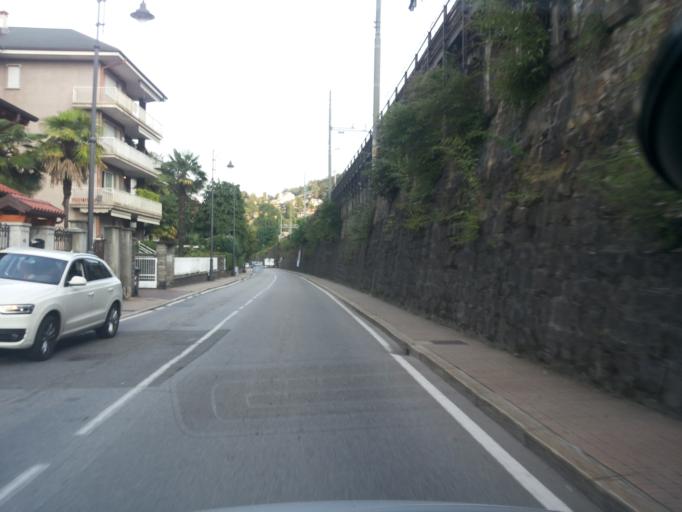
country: IT
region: Piedmont
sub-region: Provincia Verbano-Cusio-Ossola
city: Stresa
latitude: 45.8835
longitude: 8.5334
